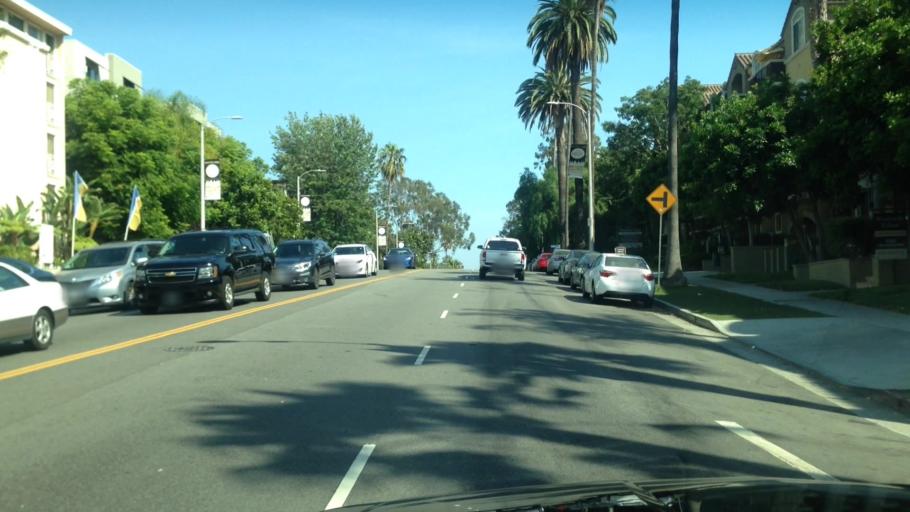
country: US
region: California
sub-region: Los Angeles County
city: Century City
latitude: 34.0499
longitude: -118.4202
